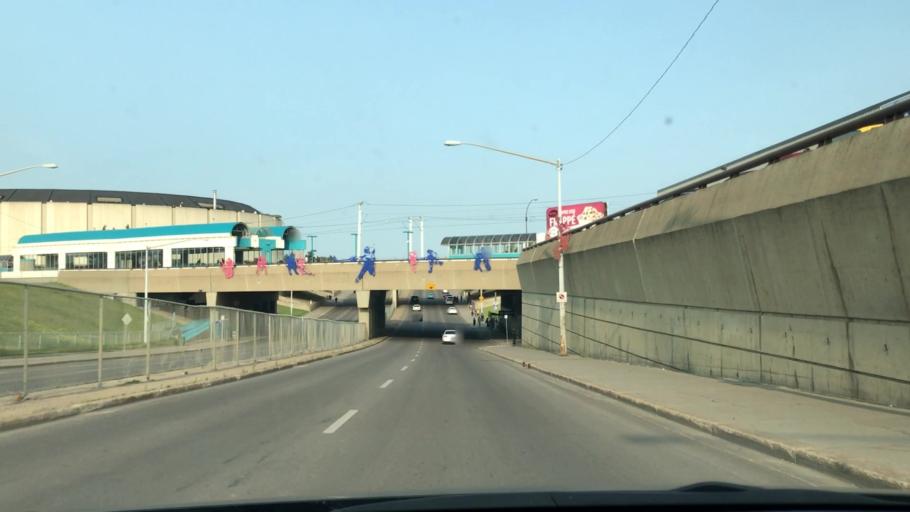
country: CA
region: Alberta
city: Edmonton
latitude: 53.5704
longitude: -113.4604
